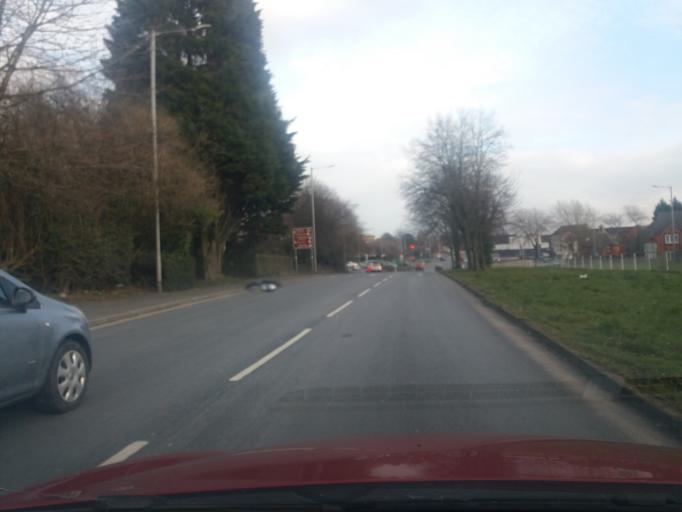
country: GB
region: England
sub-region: Lancashire
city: Preston
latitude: 53.7619
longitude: -2.6931
